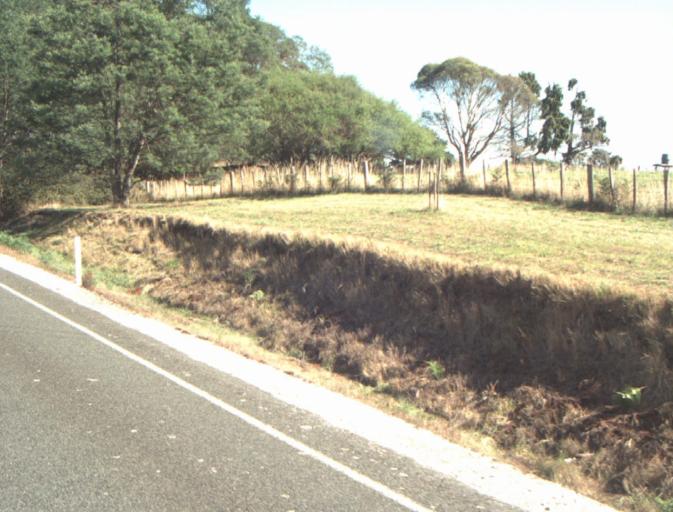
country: AU
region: Tasmania
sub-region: Launceston
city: Mayfield
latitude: -41.2848
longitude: 147.2183
